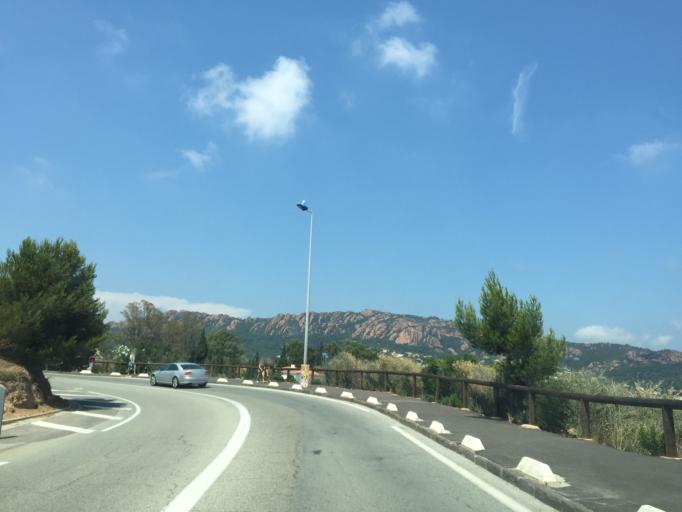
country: FR
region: Provence-Alpes-Cote d'Azur
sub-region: Departement du Var
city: Saint-Raphael
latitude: 43.4270
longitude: 6.8581
